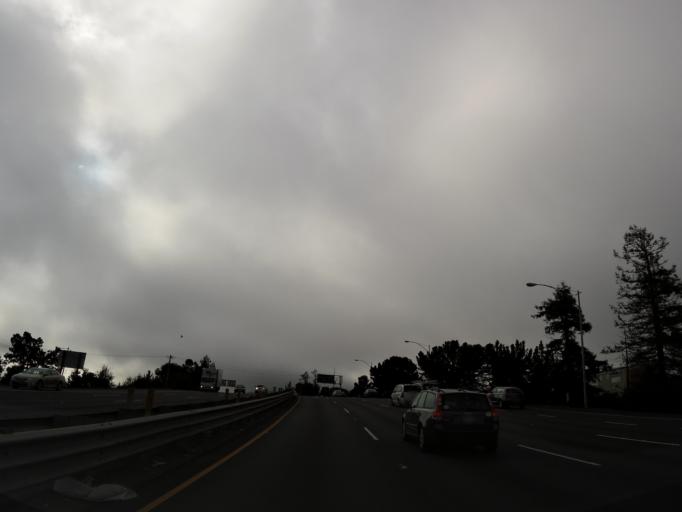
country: US
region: California
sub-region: Marin County
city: Corte Madera
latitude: 37.9374
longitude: -122.5165
